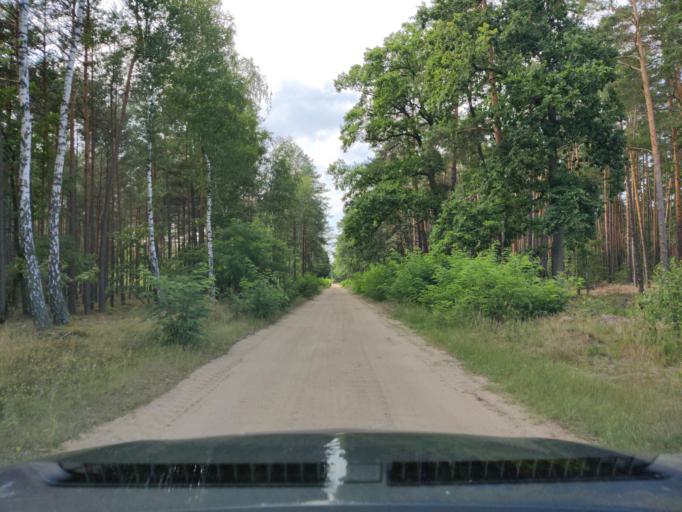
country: PL
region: Masovian Voivodeship
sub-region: Powiat pultuski
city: Pultusk
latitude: 52.6898
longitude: 21.1594
